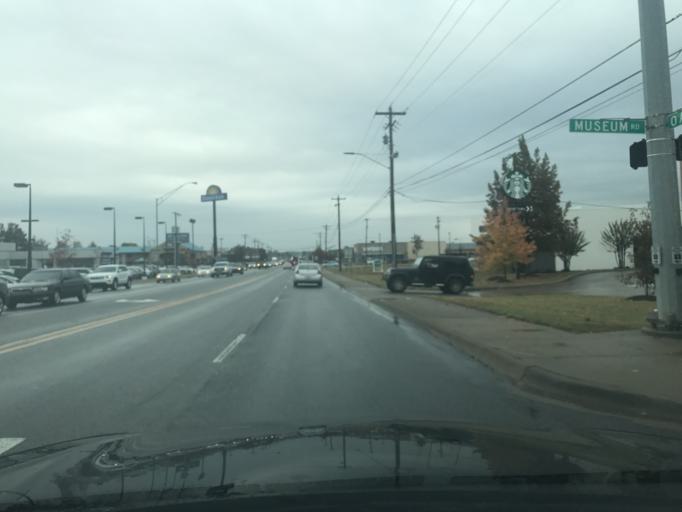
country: US
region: Arkansas
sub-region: Faulkner County
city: Conway
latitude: 35.0914
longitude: -92.4189
